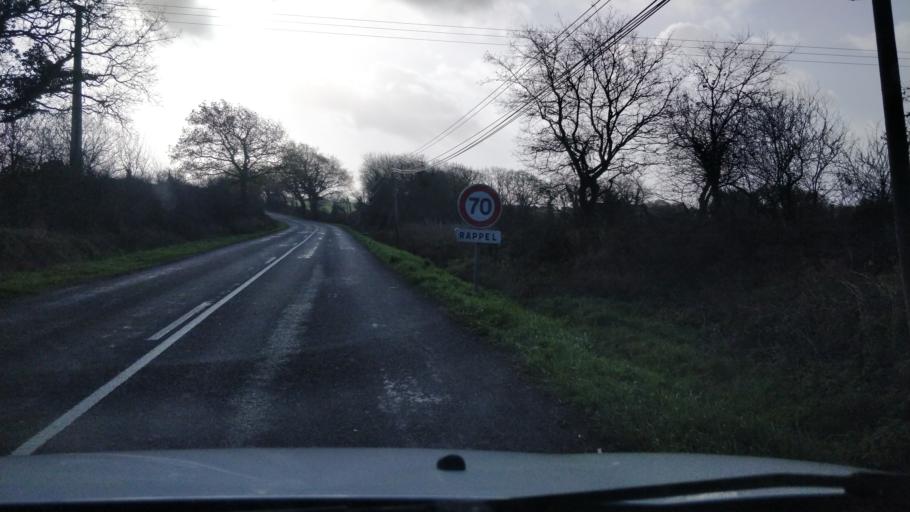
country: FR
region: Pays de la Loire
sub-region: Departement de la Loire-Atlantique
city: Guerande
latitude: 47.3485
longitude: -2.4313
